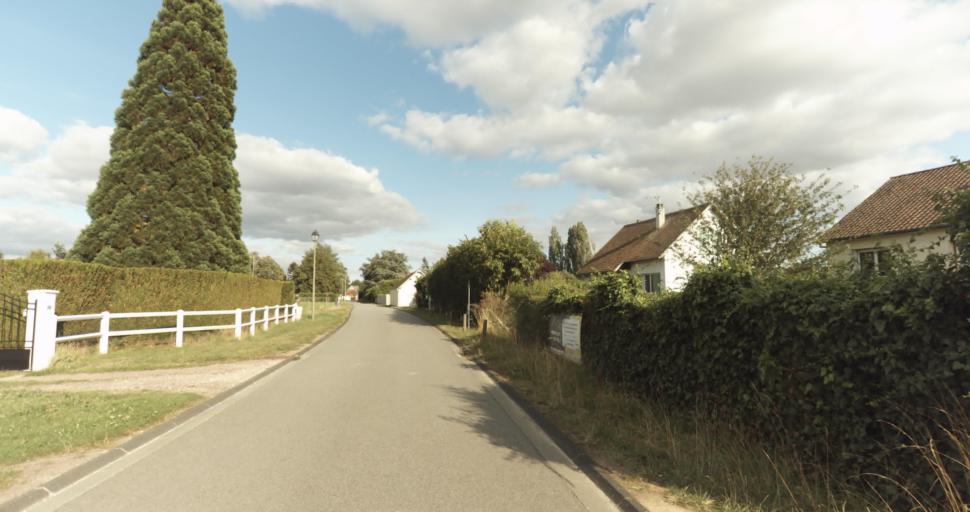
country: FR
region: Haute-Normandie
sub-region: Departement de l'Eure
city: La Couture-Boussey
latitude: 48.8965
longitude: 1.3549
